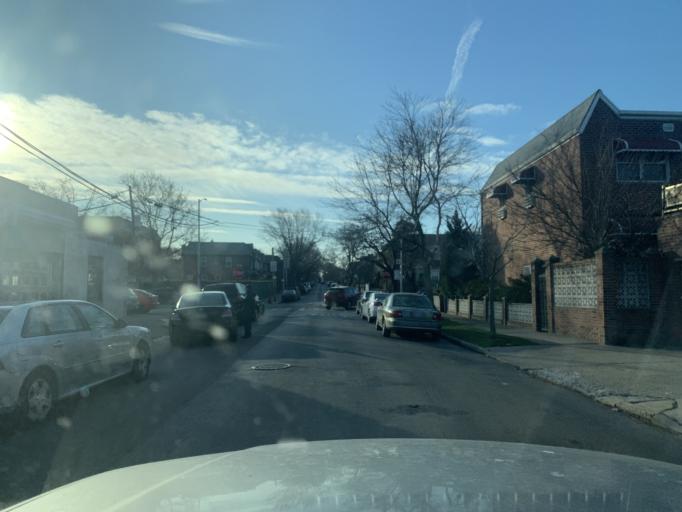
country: US
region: New York
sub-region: Queens County
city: Long Island City
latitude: 40.7593
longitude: -73.8898
